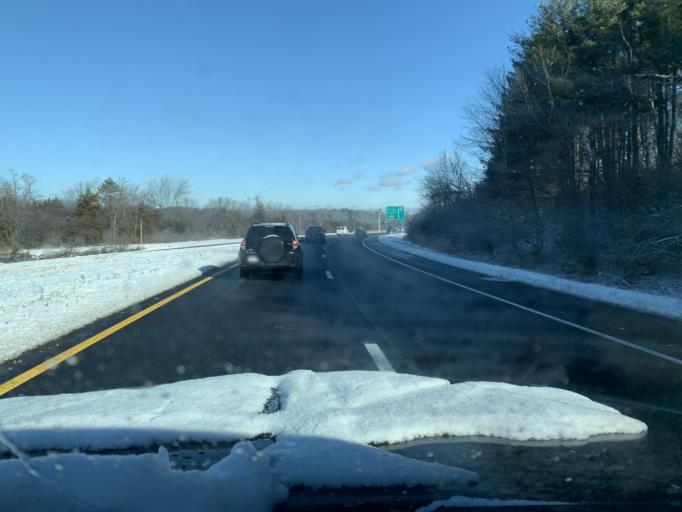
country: US
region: Massachusetts
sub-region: Essex County
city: Danvers
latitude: 42.5898
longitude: -70.9645
